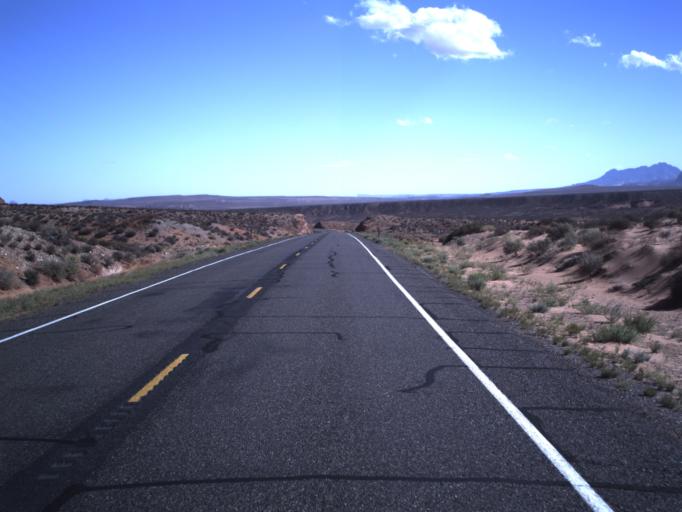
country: US
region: Utah
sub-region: Wayne County
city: Loa
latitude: 38.0772
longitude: -110.6105
